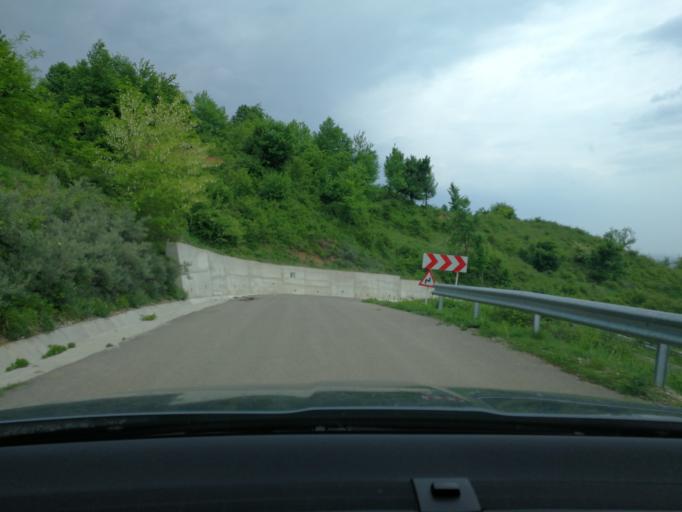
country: RO
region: Prahova
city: Cornu de Sus
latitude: 45.1718
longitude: 25.7075
